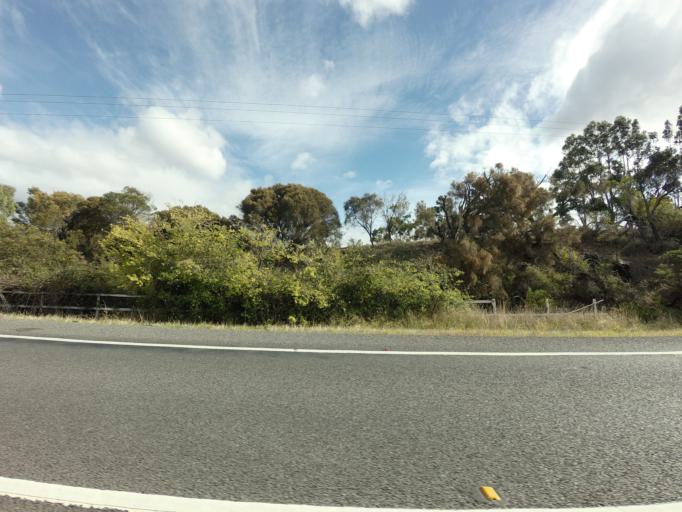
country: AU
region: Tasmania
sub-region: Glenorchy
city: Granton
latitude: -42.7446
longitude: 147.2133
